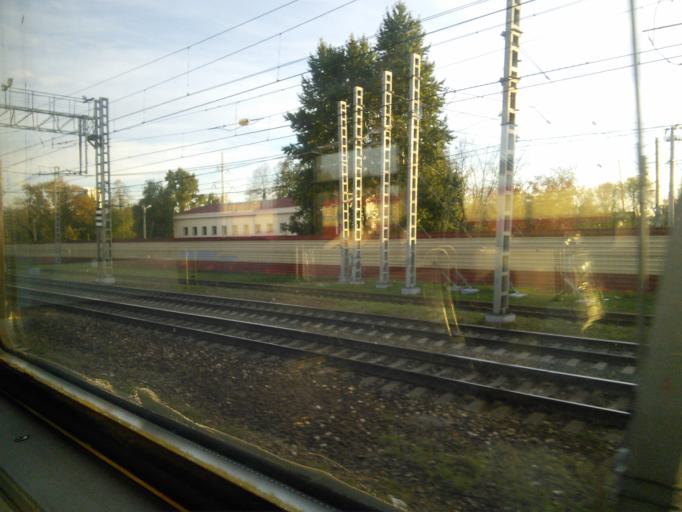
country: RU
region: Moscow
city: Ostankinskiy
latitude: 55.8153
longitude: 37.6066
